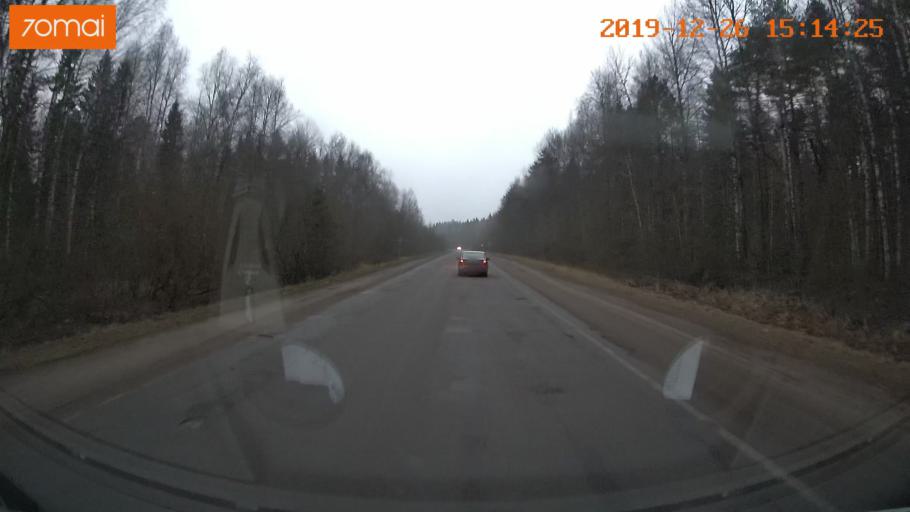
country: RU
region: Jaroslavl
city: Rybinsk
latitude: 58.1062
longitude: 38.8807
